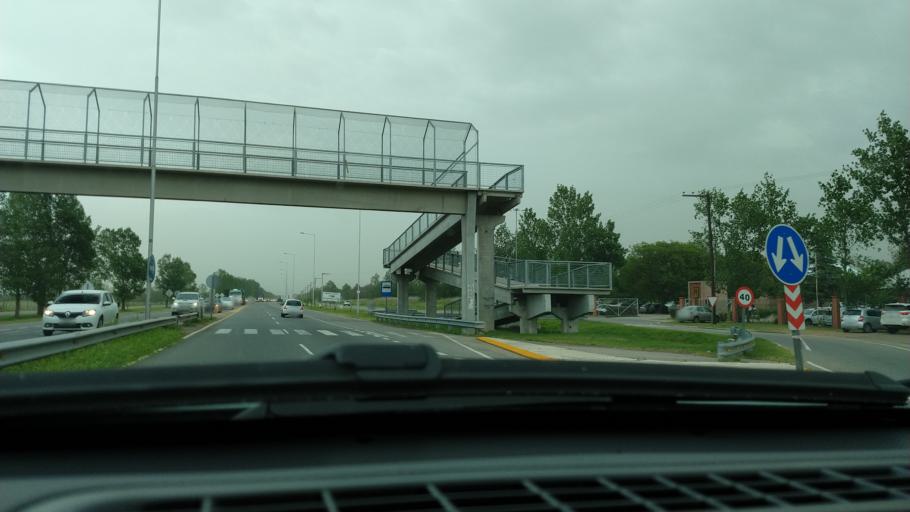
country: AR
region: Cordoba
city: Villa Allende
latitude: -31.3038
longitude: -64.2262
